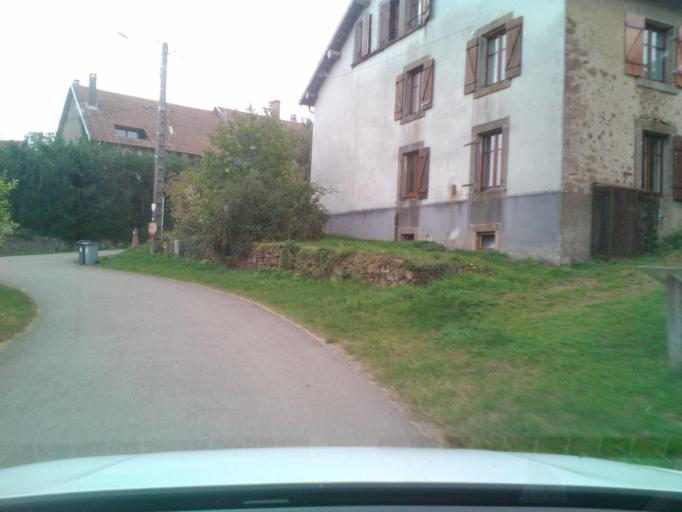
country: FR
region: Lorraine
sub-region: Departement des Vosges
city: Senones
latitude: 48.3475
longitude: 6.9942
